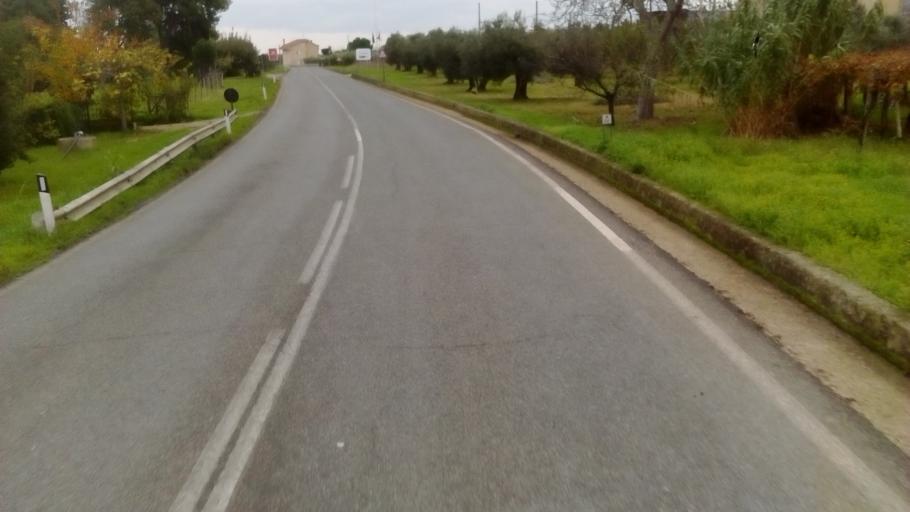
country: IT
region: Abruzzo
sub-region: Provincia di Chieti
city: Vasto
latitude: 42.1654
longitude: 14.6658
